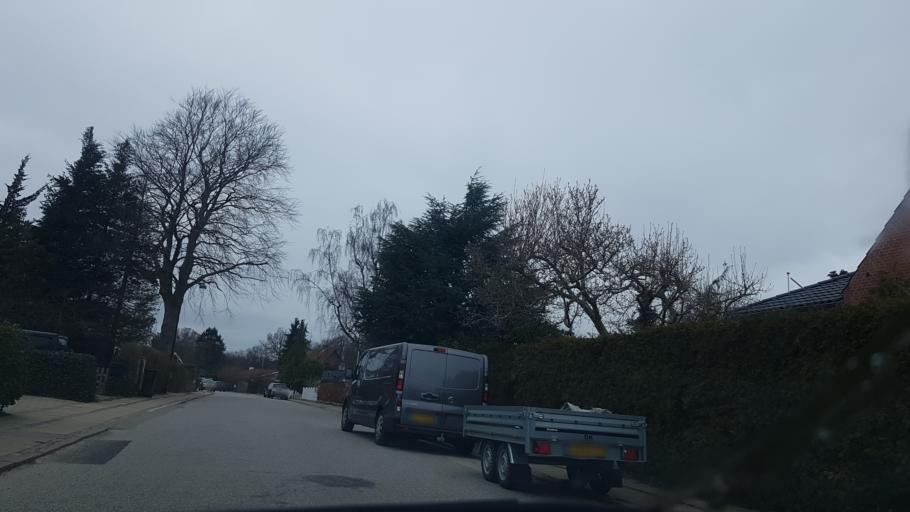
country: DK
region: Capital Region
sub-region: Lyngby-Tarbaek Kommune
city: Kongens Lyngby
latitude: 55.7512
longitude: 12.5082
